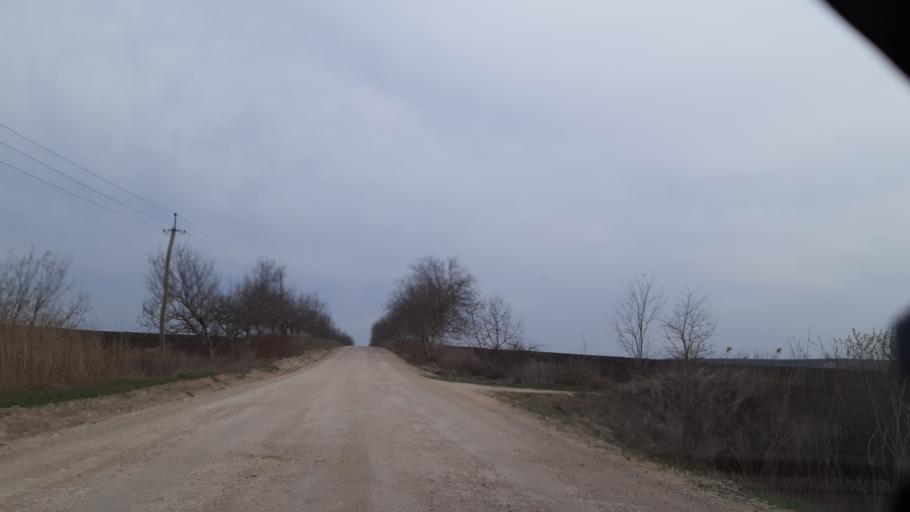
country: MD
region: Soldanesti
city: Soldanesti
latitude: 47.6972
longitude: 28.7290
